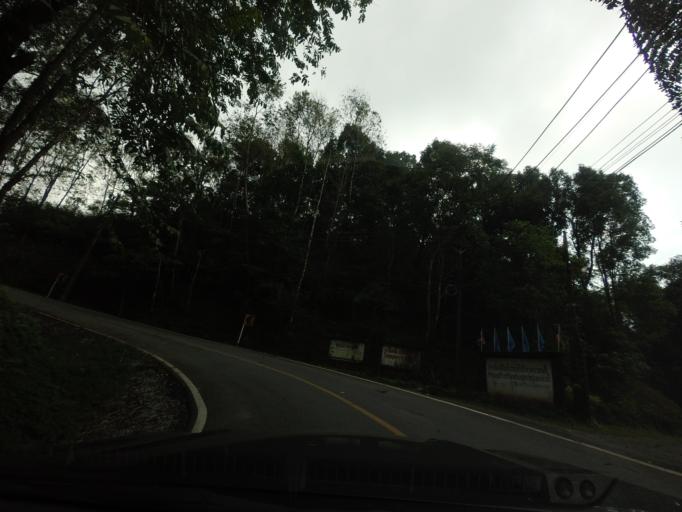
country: TH
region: Nan
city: Bo Kluea
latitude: 19.1833
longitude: 101.0745
